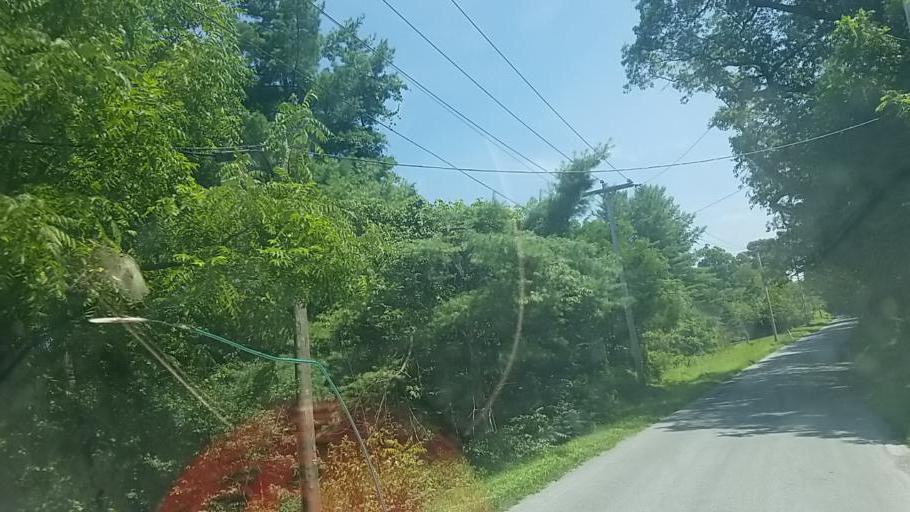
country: US
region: Pennsylvania
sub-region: Chester County
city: Atglen
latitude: 39.8888
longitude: -75.9454
